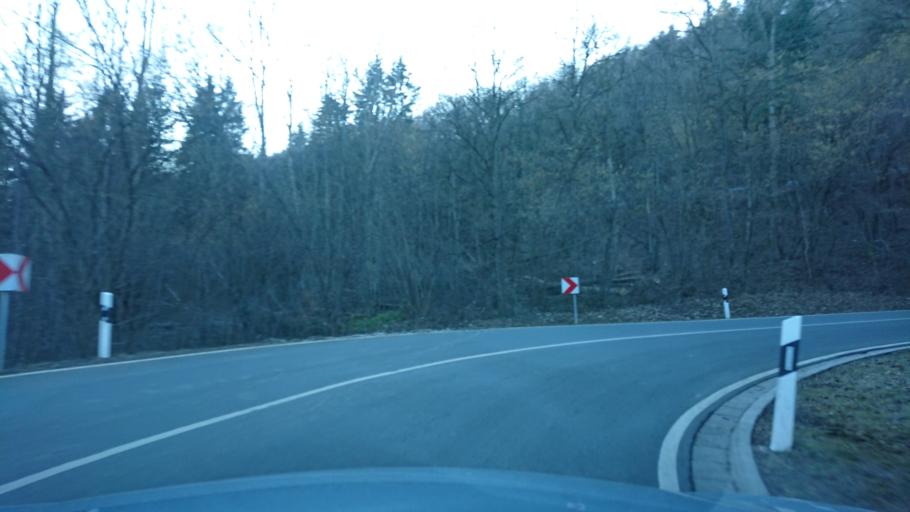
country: DE
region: Bavaria
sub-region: Upper Franconia
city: Ebermannstadt
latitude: 49.7873
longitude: 11.1717
